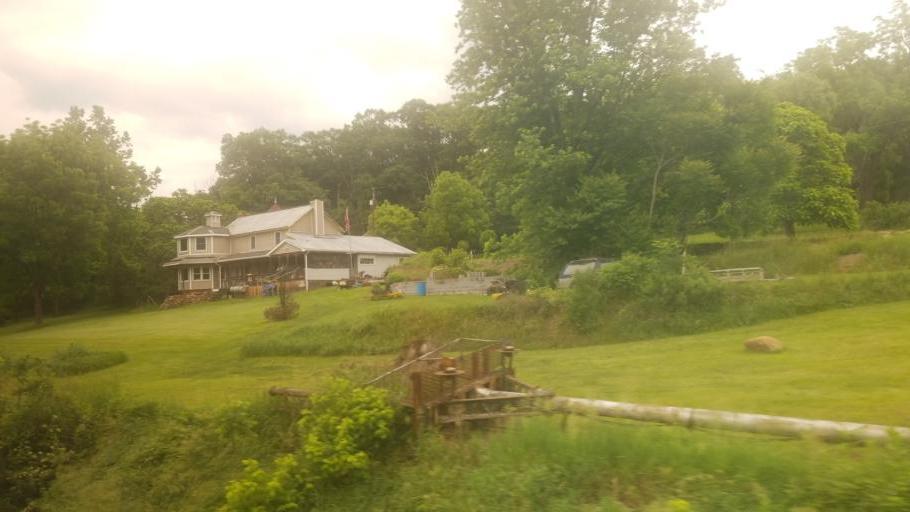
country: US
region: West Virginia
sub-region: Morgan County
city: Berkeley Springs
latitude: 39.6180
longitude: -78.3754
